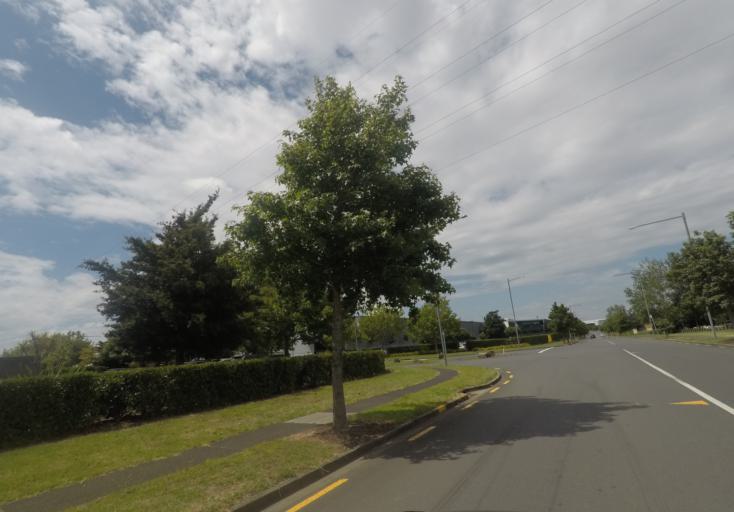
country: NZ
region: Auckland
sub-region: Auckland
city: Manukau City
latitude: -36.9434
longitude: 174.8732
